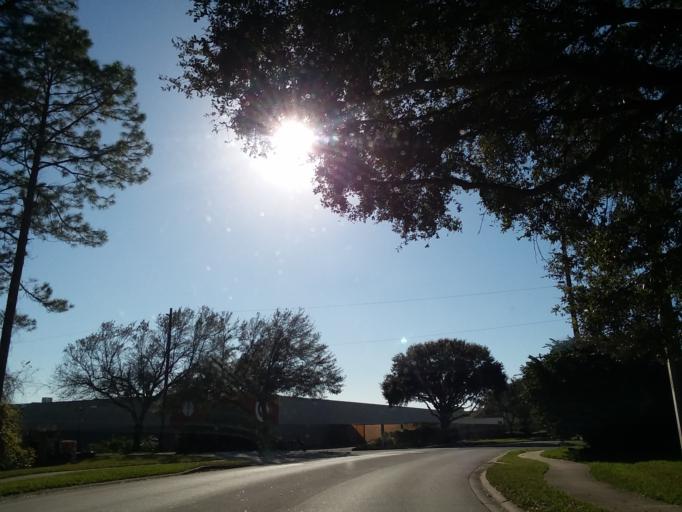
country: US
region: Florida
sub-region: Saint Johns County
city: Fruit Cove
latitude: 30.1950
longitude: -81.5475
